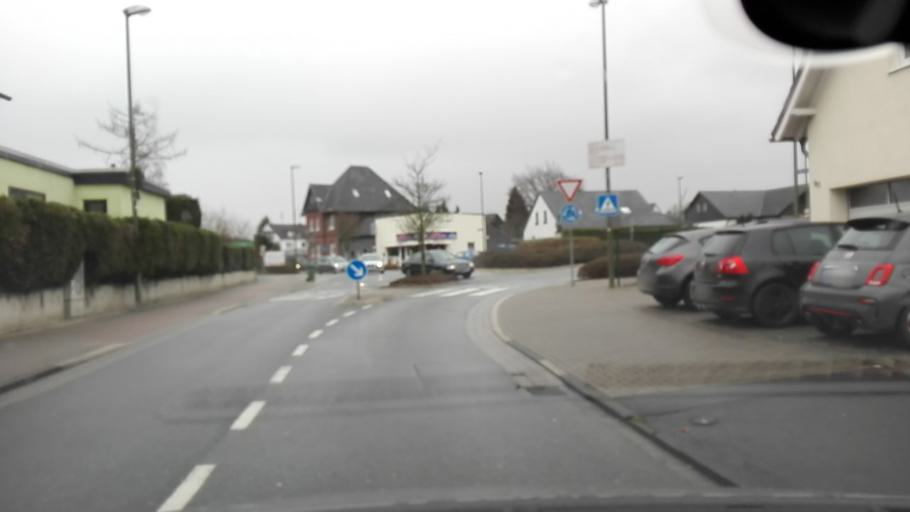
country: DE
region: North Rhine-Westphalia
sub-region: Regierungsbezirk Arnsberg
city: Bonen
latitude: 51.5813
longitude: 7.7250
